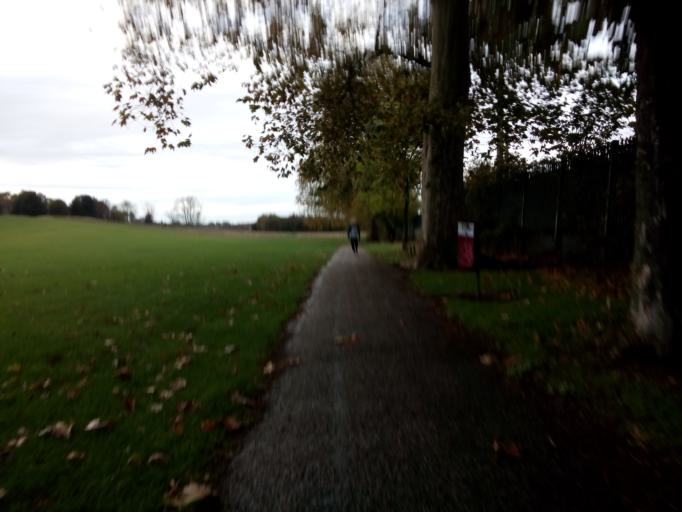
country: GB
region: England
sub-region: Suffolk
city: Ipswich
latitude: 52.0520
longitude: 1.1369
